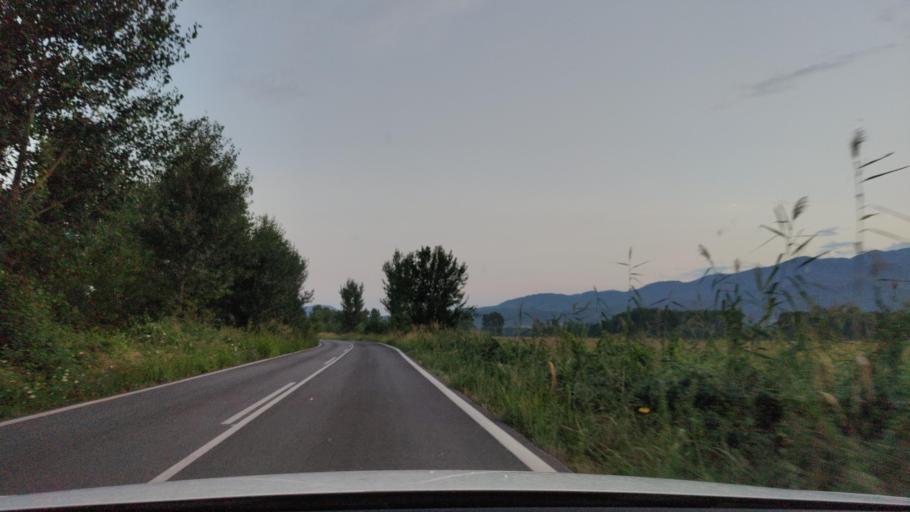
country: GR
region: Central Macedonia
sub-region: Nomos Serron
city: Chrysochorafa
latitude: 41.1538
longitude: 23.2400
